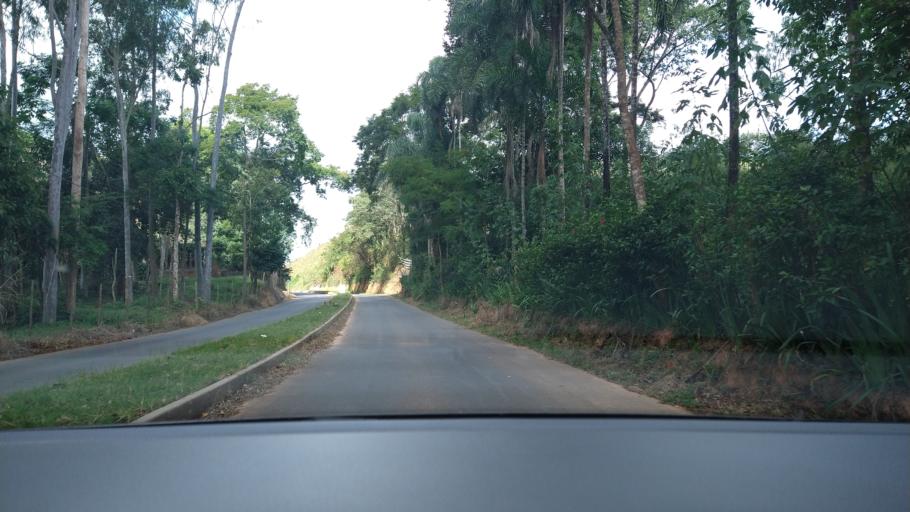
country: BR
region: Minas Gerais
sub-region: Vicosa
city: Vicosa
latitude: -20.7809
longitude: -42.8509
